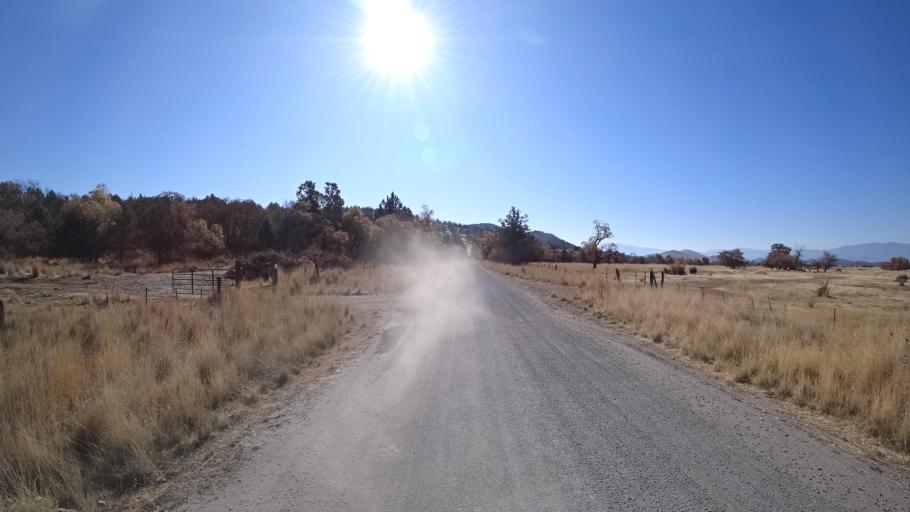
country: US
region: California
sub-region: Siskiyou County
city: Montague
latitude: 41.7242
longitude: -122.3696
